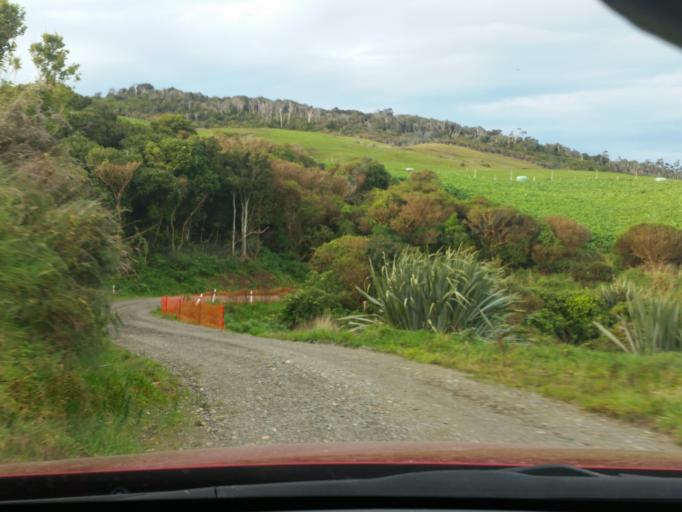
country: NZ
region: Southland
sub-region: Southland District
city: Riverton
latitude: -46.2975
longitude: 167.7807
